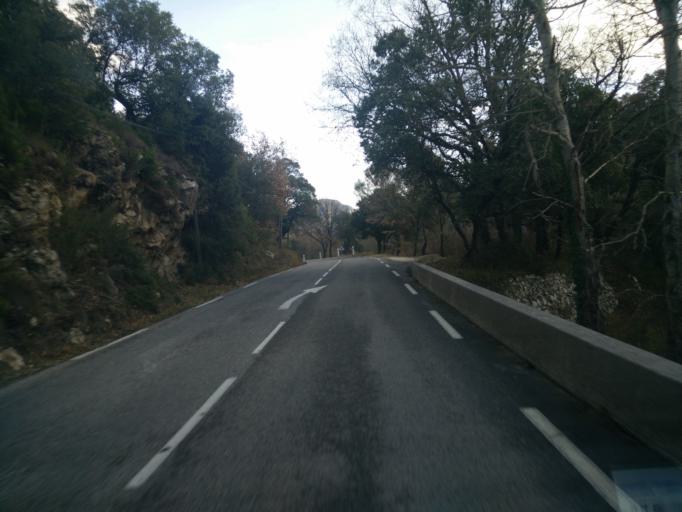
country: FR
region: Provence-Alpes-Cote d'Azur
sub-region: Departement du Var
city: Signes
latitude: 43.2824
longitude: 5.8992
